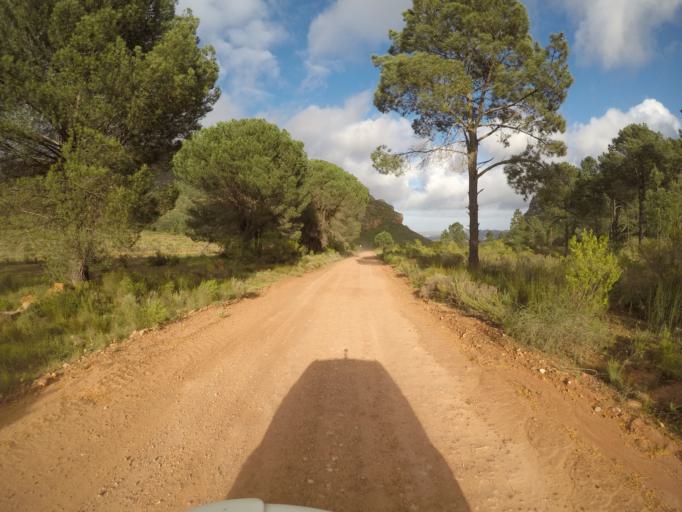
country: ZA
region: Western Cape
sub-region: West Coast District Municipality
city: Clanwilliam
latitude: -32.3411
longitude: 18.7952
